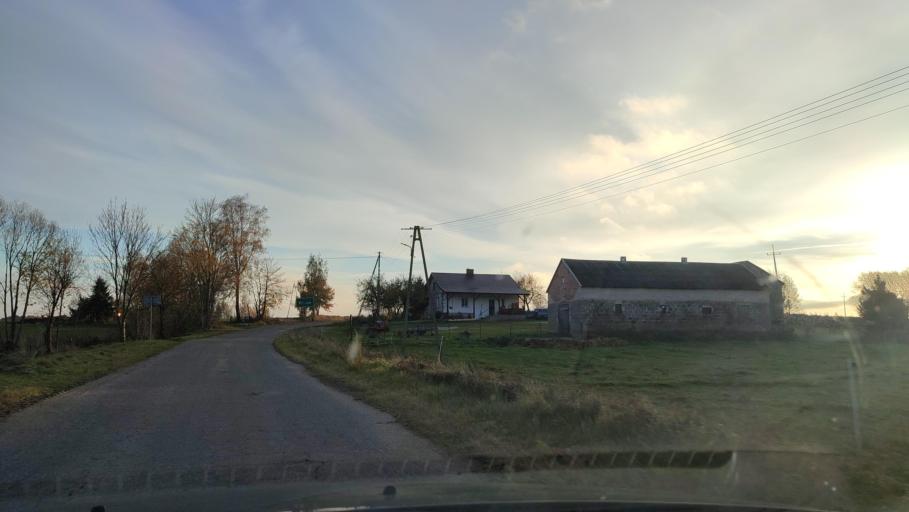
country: PL
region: Masovian Voivodeship
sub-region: Powiat mlawski
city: Wieczfnia Koscielna
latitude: 53.2434
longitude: 20.5808
